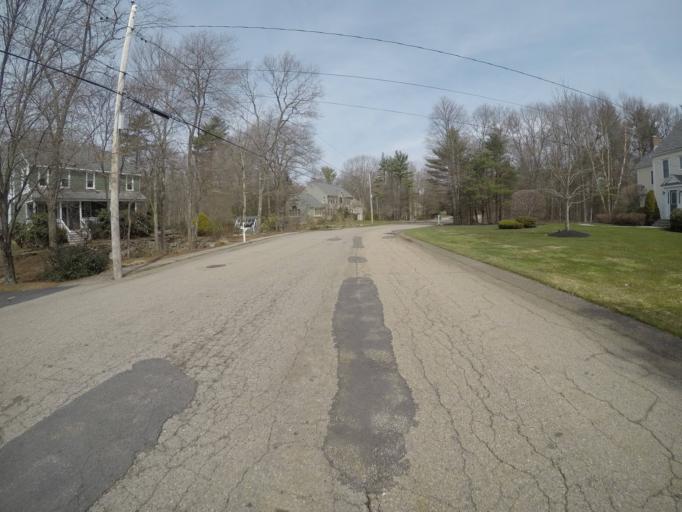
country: US
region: Massachusetts
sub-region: Bristol County
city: Easton
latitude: 42.0418
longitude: -71.1078
